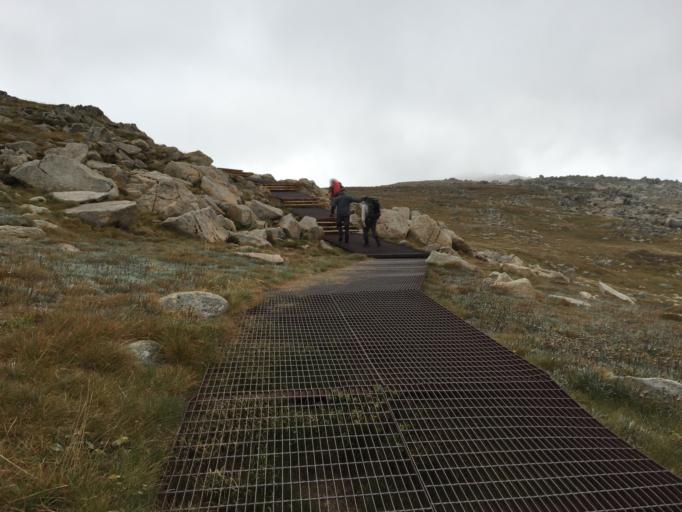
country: AU
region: New South Wales
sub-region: Snowy River
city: Jindabyne
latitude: -36.4664
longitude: 148.2700
